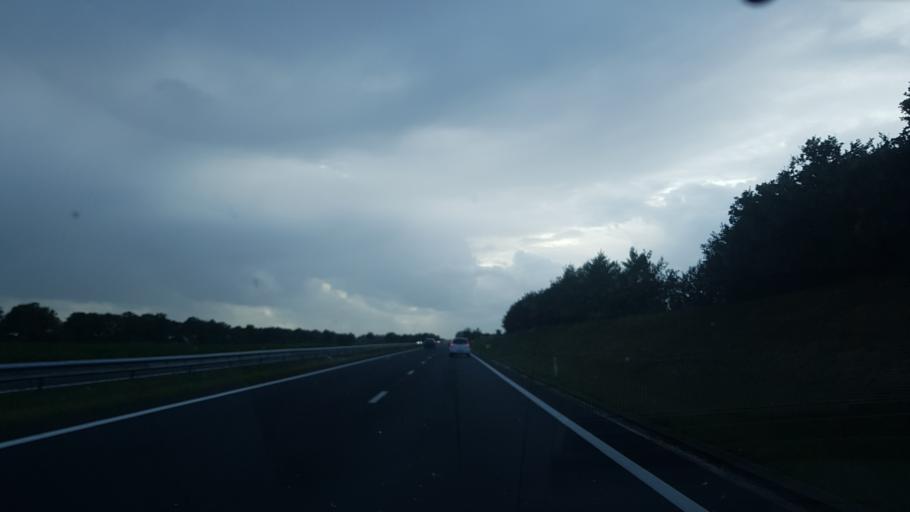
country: NL
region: Friesland
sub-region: Gemeente Smallingerland
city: Oudega
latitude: 53.1470
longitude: 5.9900
